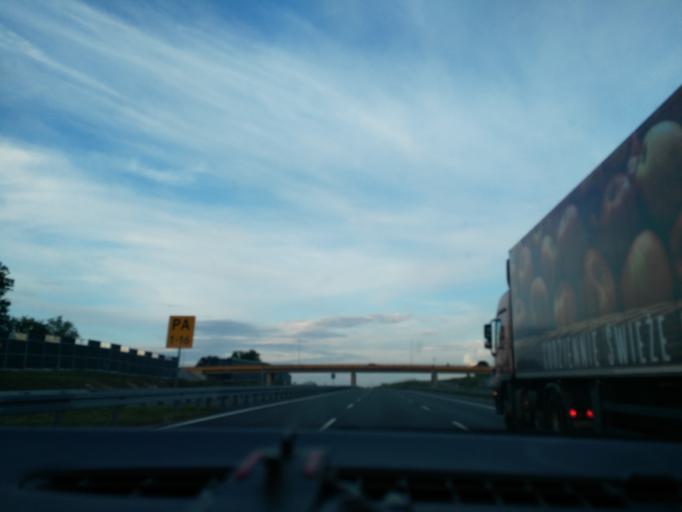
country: PL
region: Lublin Voivodeship
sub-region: Powiat lubelski
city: Lublin
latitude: 51.2979
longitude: 22.5390
